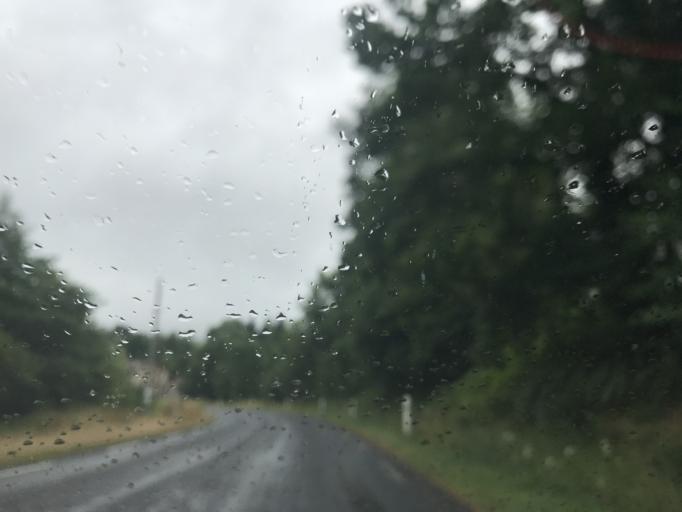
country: FR
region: Auvergne
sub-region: Departement du Puy-de-Dome
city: Job
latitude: 45.6142
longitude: 3.7221
